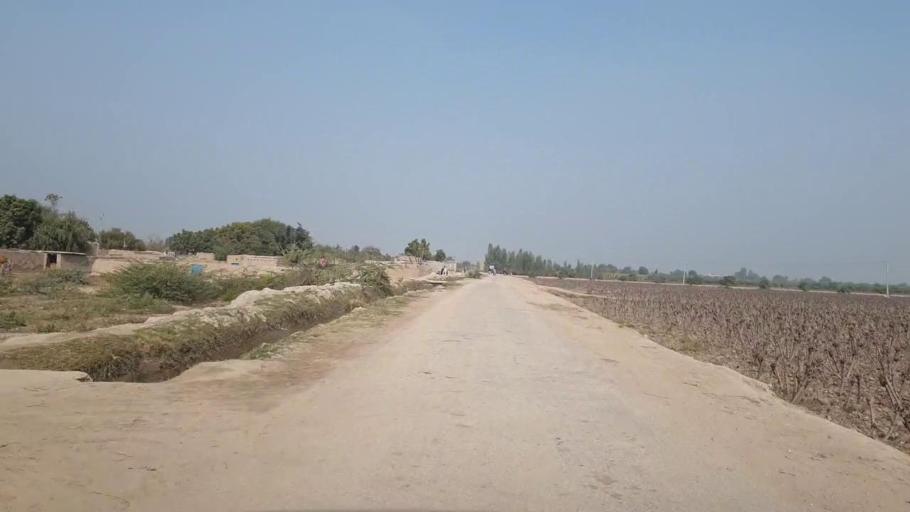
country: PK
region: Sindh
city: Bhit Shah
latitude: 25.7902
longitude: 68.4930
